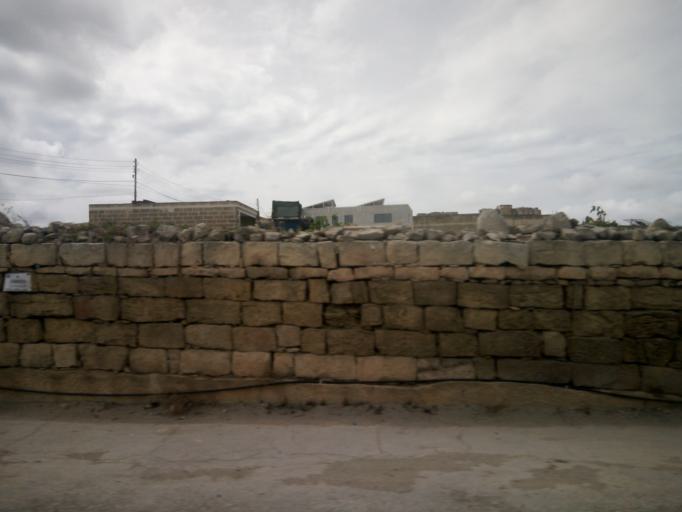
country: MT
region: Luqa
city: Luqa
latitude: 35.8651
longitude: 14.4902
